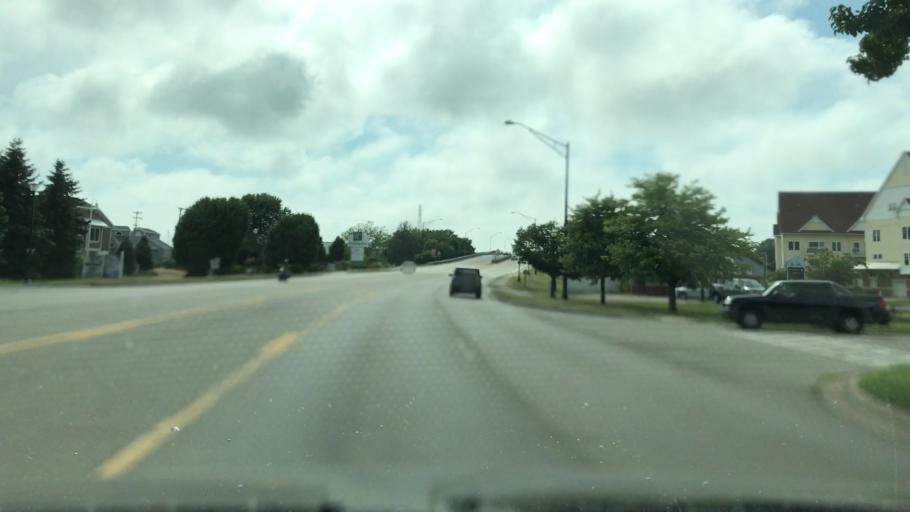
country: US
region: Michigan
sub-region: Ottawa County
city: Spring Lake
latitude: 43.0764
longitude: -86.2088
